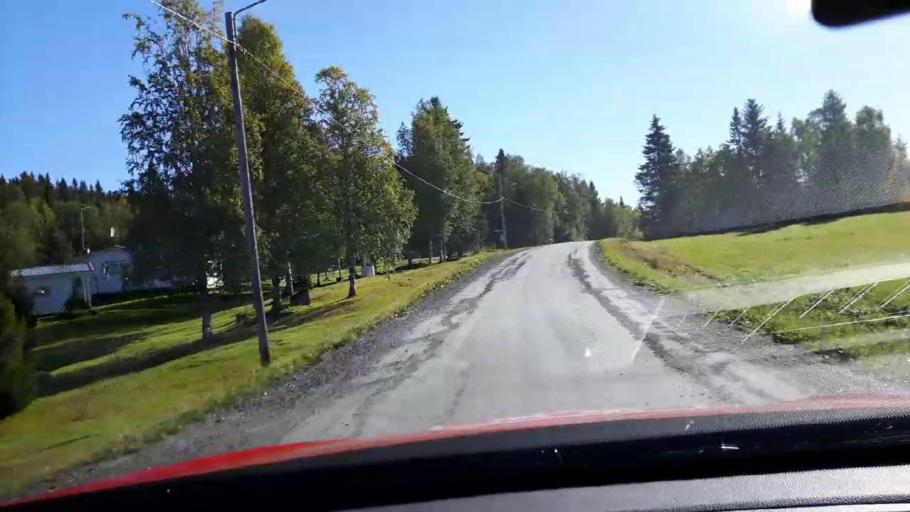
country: NO
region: Nord-Trondelag
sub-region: Lierne
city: Sandvika
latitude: 64.6441
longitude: 13.7787
